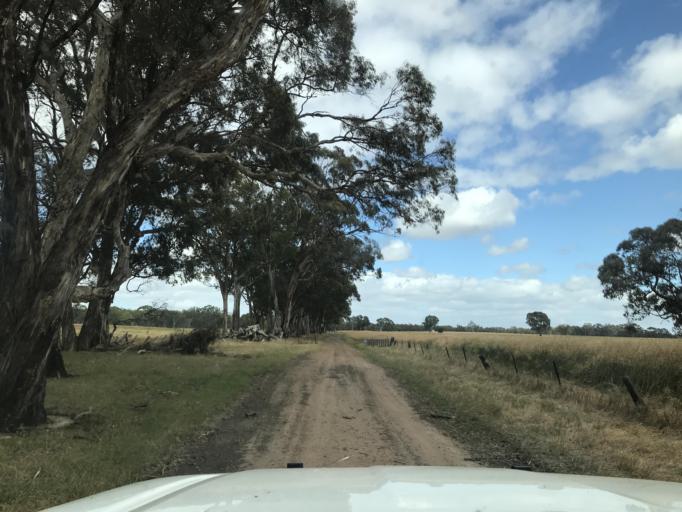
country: AU
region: South Australia
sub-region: Naracoorte and Lucindale
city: Naracoorte
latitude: -36.8980
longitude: 141.3779
